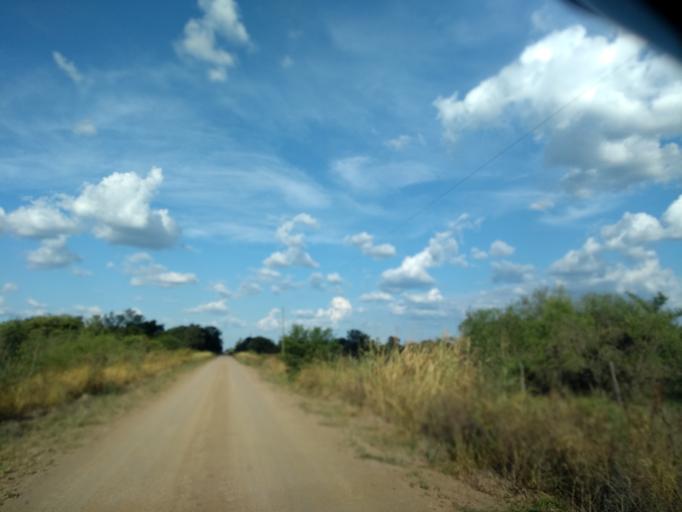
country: AR
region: Chaco
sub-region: Departamento de Quitilipi
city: Quitilipi
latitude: -26.7472
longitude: -60.2709
